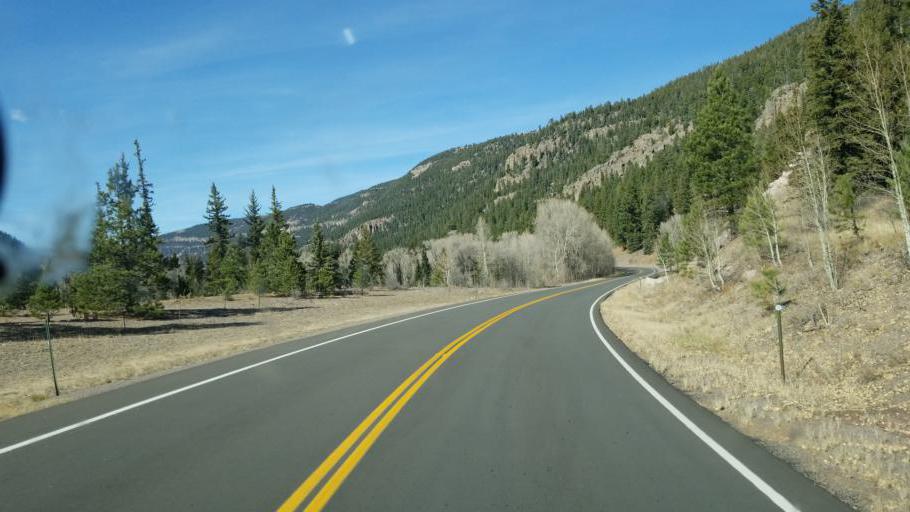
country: US
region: Colorado
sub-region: Conejos County
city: Conejos
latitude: 37.0873
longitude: -106.3025
